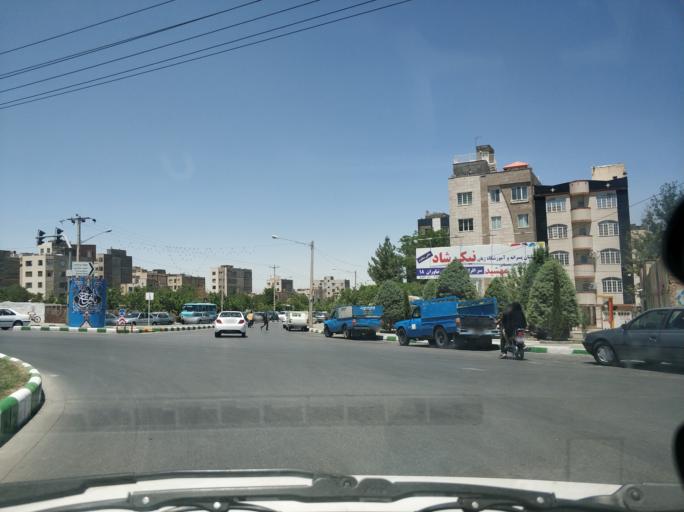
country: IR
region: Razavi Khorasan
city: Mashhad
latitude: 36.3007
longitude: 59.5107
